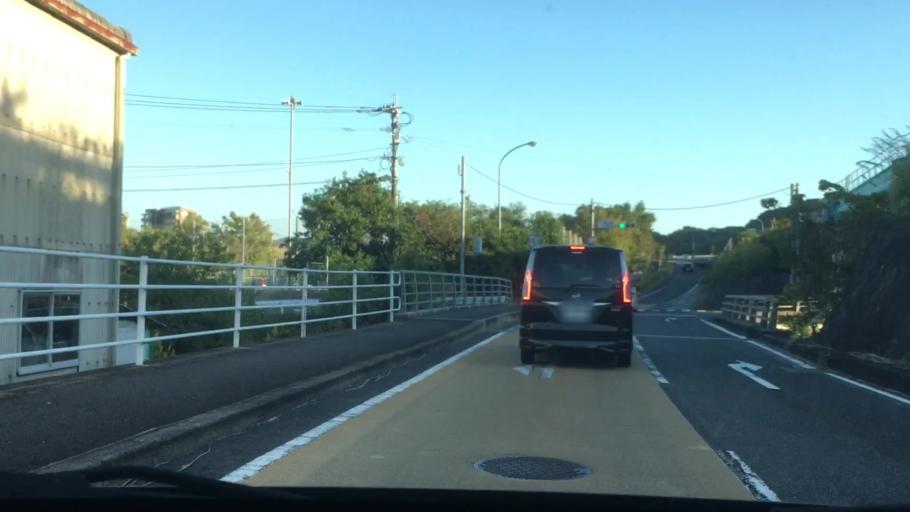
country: JP
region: Nagasaki
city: Sasebo
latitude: 33.1457
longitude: 129.7787
